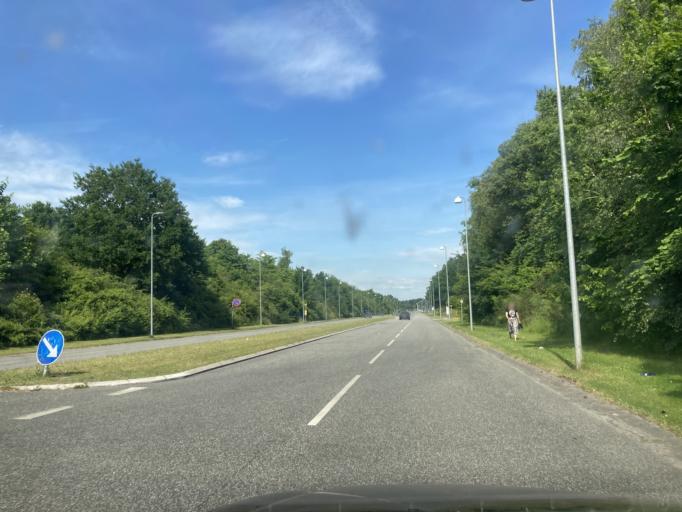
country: DK
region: Capital Region
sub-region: Hillerod Kommune
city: Hillerod
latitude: 55.9314
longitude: 12.3473
